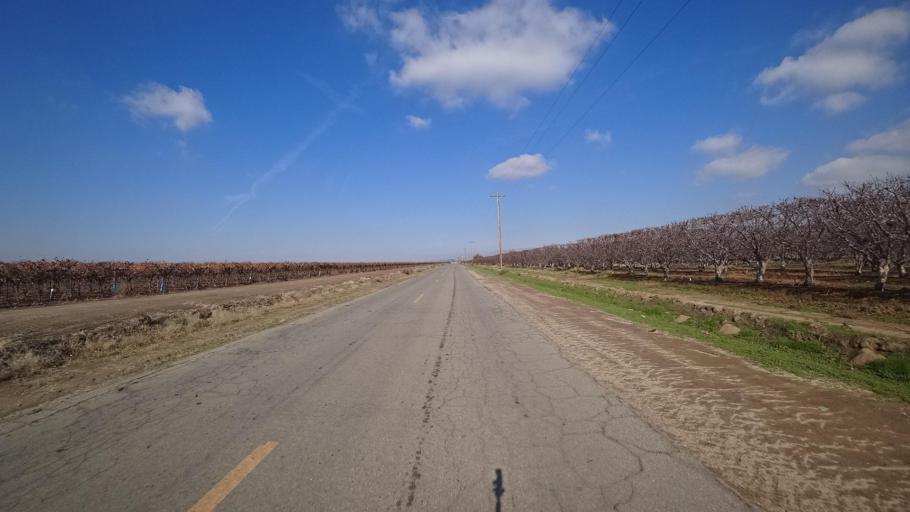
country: US
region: California
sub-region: Kern County
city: Arvin
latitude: 35.2461
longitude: -118.7885
